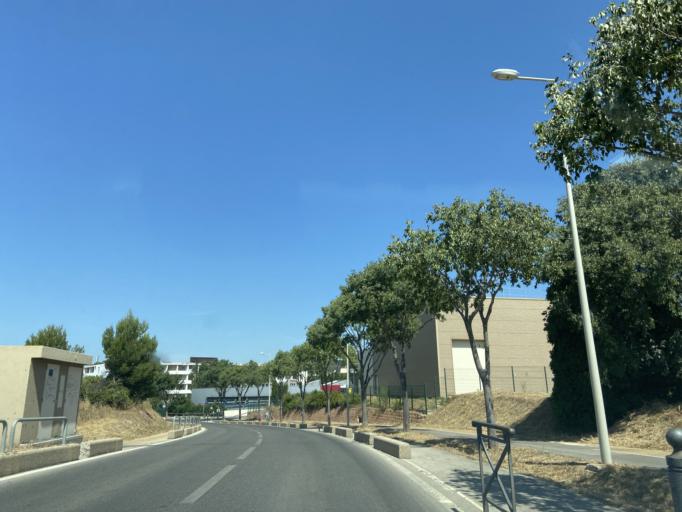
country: FR
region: Provence-Alpes-Cote d'Azur
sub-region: Departement des Bouches-du-Rhone
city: Plan-de-Cuques
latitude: 43.3438
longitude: 5.4445
